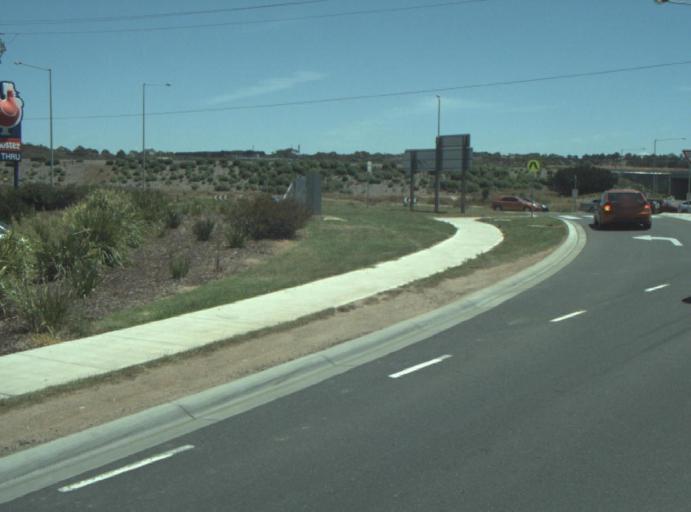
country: AU
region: Victoria
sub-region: Greater Geelong
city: Wandana Heights
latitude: -38.2014
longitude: 144.3120
